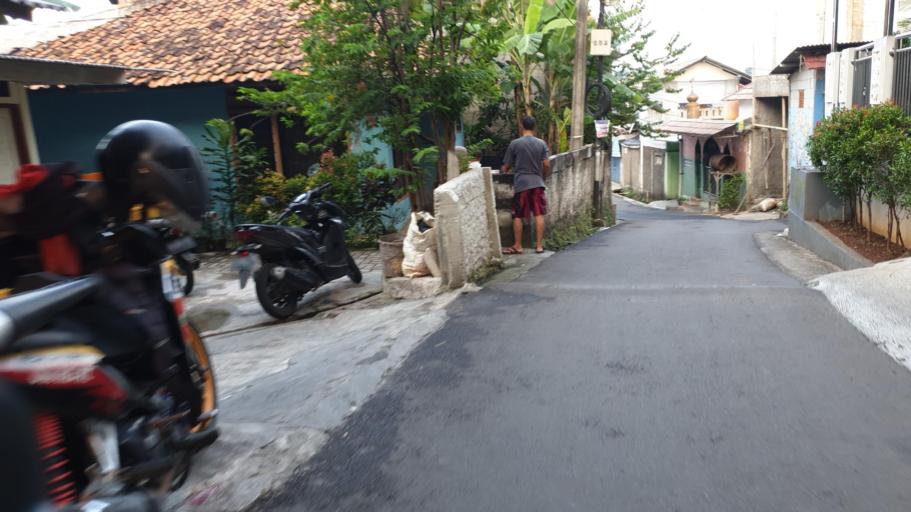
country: ID
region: West Java
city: Depok
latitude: -6.3287
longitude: 106.8306
